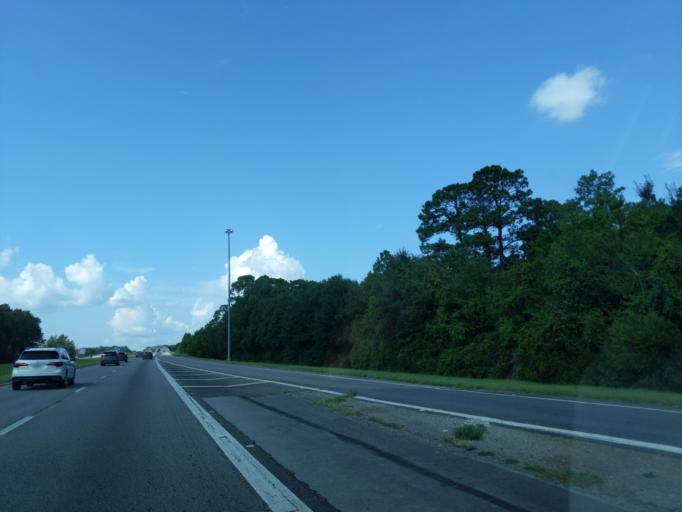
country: US
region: Florida
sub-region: Santa Rosa County
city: Bagdad
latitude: 30.5903
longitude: -87.0057
